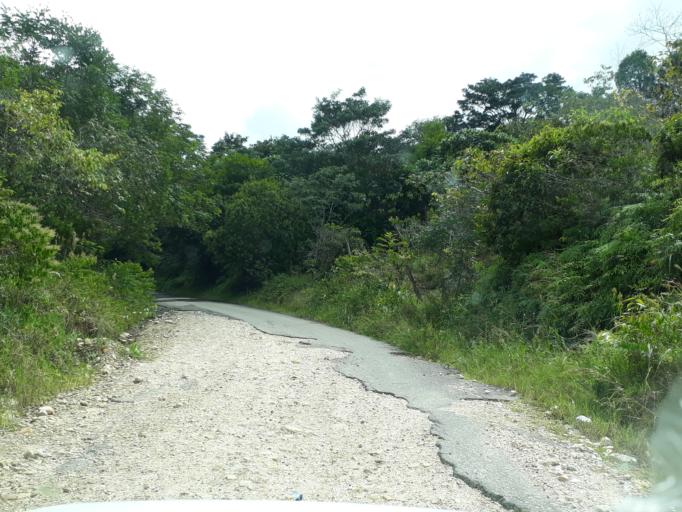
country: CO
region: Cundinamarca
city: Medina
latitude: 4.5783
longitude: -73.3435
